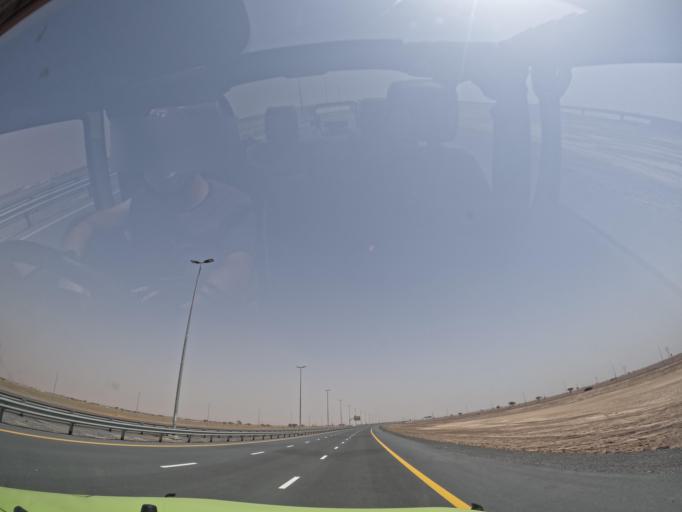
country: AE
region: Ash Shariqah
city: Adh Dhayd
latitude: 24.9123
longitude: 55.8013
